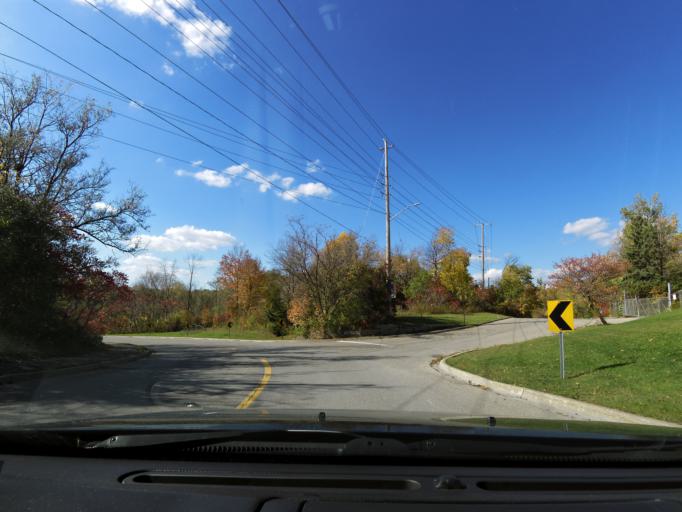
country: CA
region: Ontario
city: Hamilton
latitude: 43.3060
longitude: -79.8601
